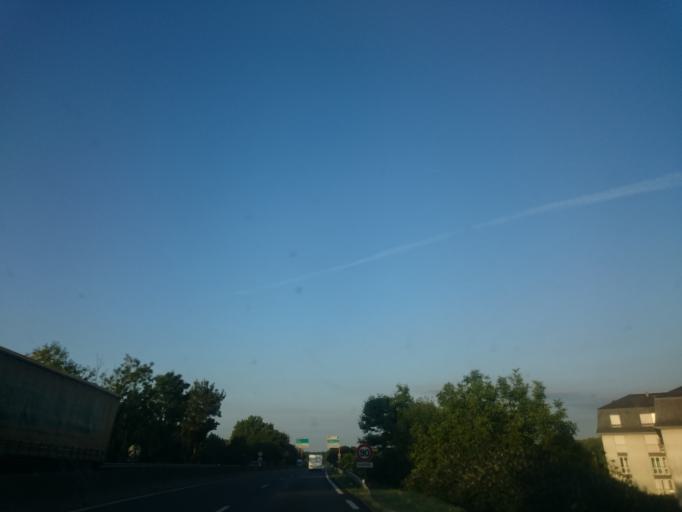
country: FR
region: Ile-de-France
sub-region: Departement de l'Essonne
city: Etampes
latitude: 48.4264
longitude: 2.1481
